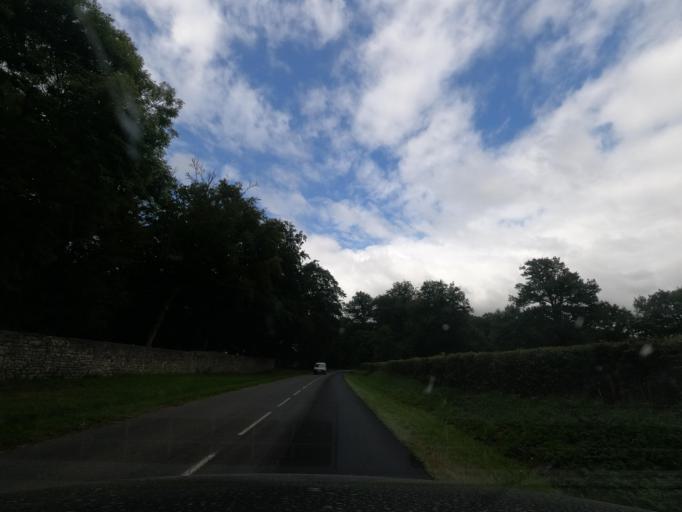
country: FR
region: Lower Normandy
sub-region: Departement de l'Orne
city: Briouze
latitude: 48.7250
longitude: -0.3473
